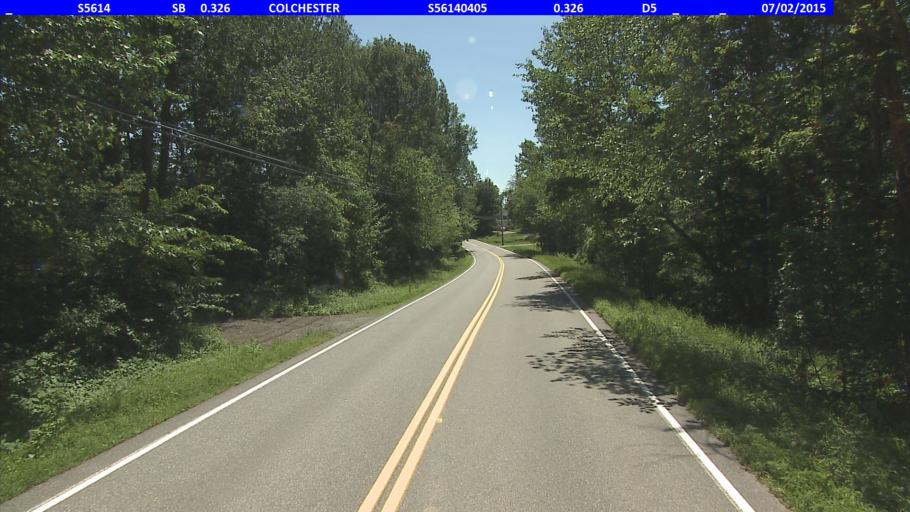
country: US
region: Vermont
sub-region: Chittenden County
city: Colchester
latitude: 44.5268
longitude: -73.1521
